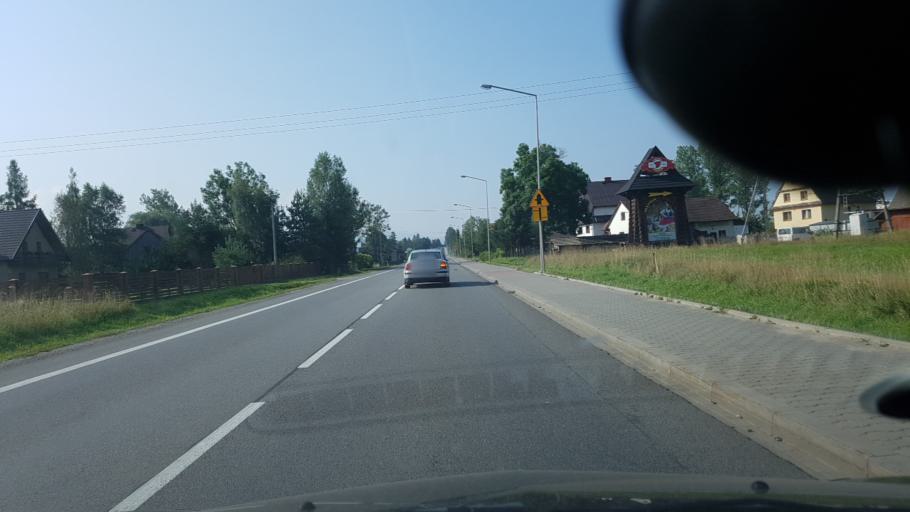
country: PL
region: Lesser Poland Voivodeship
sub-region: Powiat nowotarski
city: Jablonka
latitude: 49.4662
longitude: 19.6916
